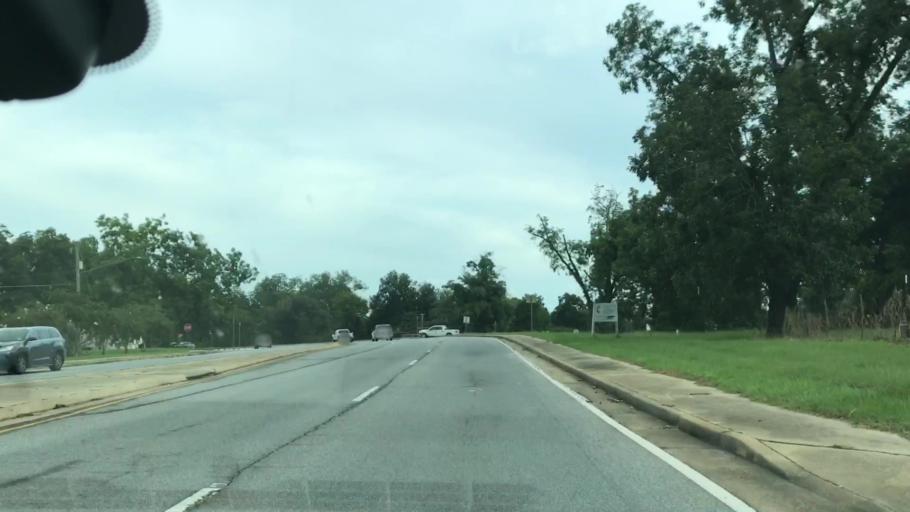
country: US
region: Georgia
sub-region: Quitman County
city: Georgetown
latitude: 31.8860
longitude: -85.1059
